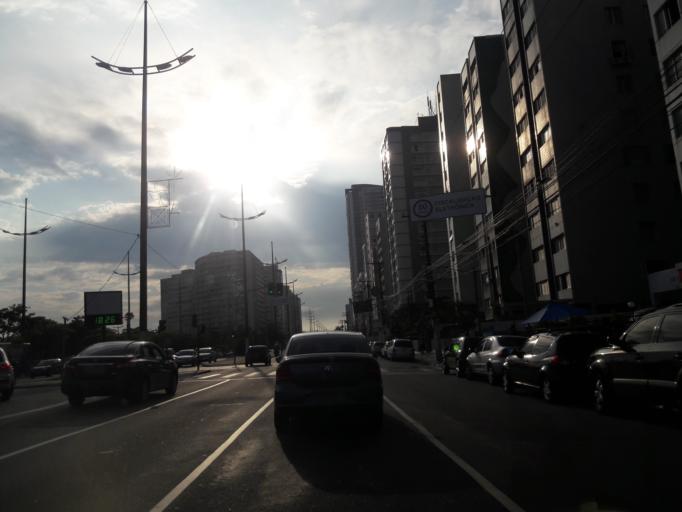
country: BR
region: Sao Paulo
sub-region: Santos
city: Santos
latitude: -23.9679
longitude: -46.3492
